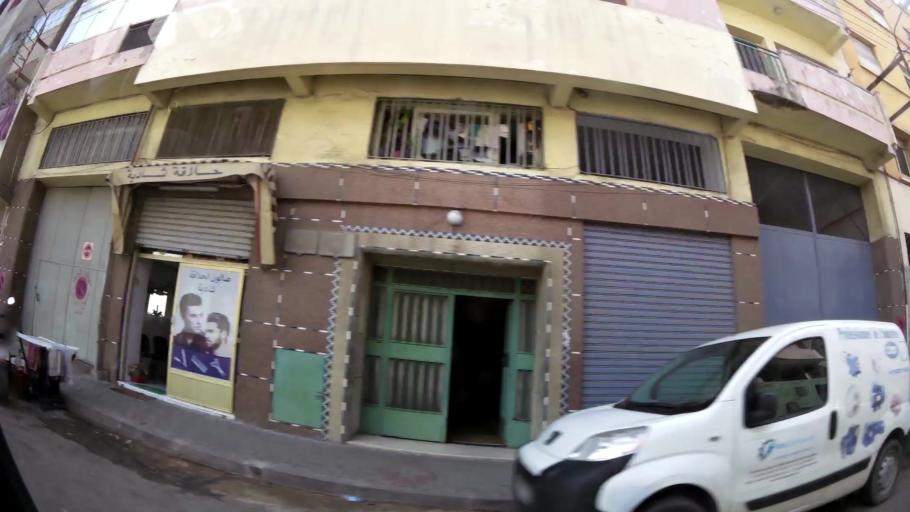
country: MA
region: Grand Casablanca
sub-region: Casablanca
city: Casablanca
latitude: 33.5871
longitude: -7.5797
